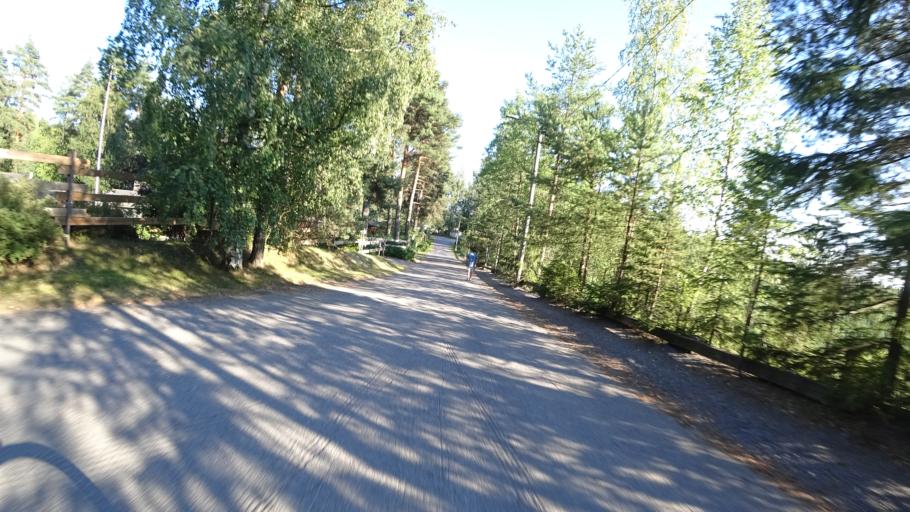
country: FI
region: Pirkanmaa
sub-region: Tampere
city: Pirkkala
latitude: 61.4959
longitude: 23.6099
